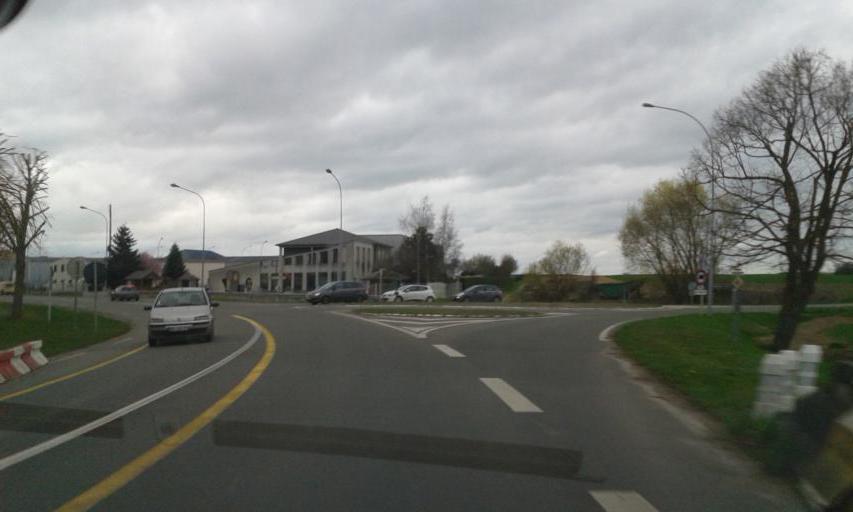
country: FR
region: Centre
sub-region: Departement d'Eure-et-Loir
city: Leves
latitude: 48.4839
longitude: 1.4790
